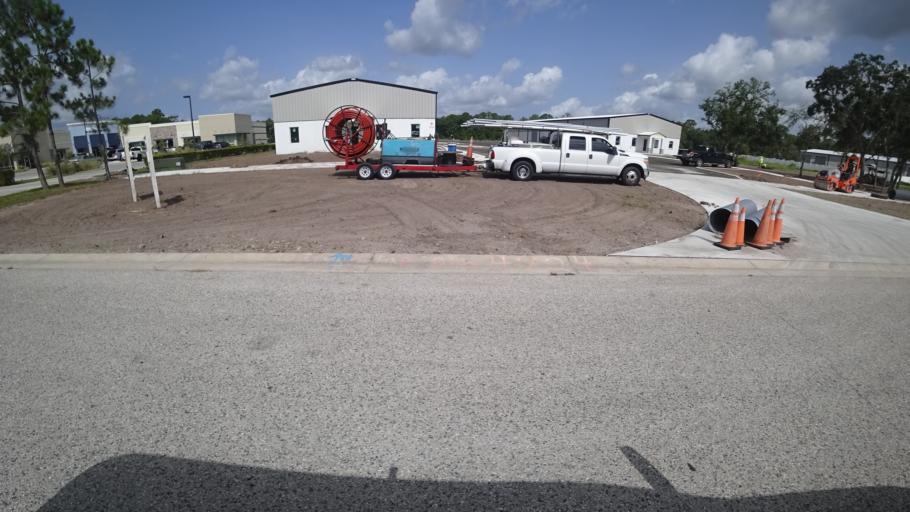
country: US
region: Florida
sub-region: Manatee County
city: Samoset
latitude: 27.4554
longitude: -82.4564
